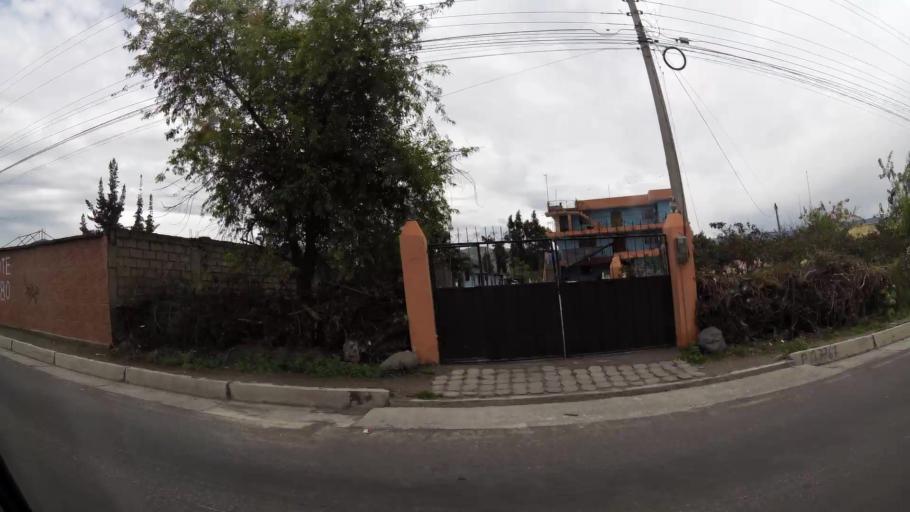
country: EC
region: Cotopaxi
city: San Miguel de Salcedo
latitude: -1.0270
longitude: -78.5912
